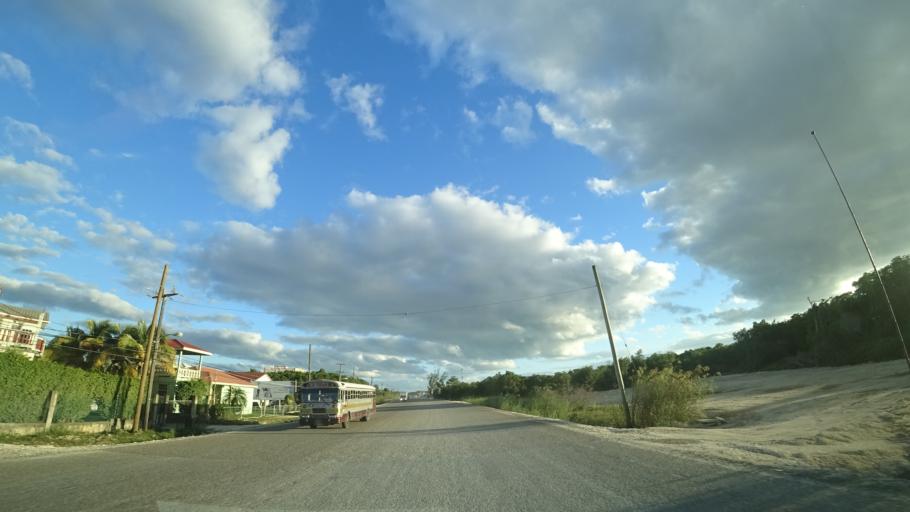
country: BZ
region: Belize
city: Belize City
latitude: 17.5291
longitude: -88.2391
